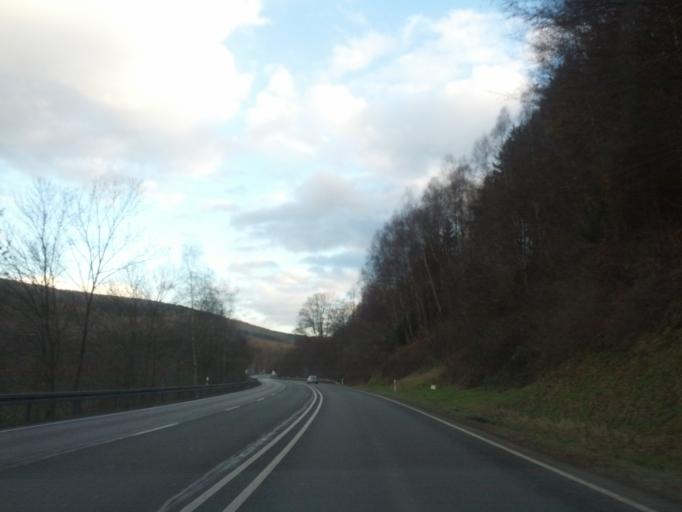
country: DE
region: Hesse
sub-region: Regierungsbezirk Kassel
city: Helsa
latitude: 51.2749
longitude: 9.6530
